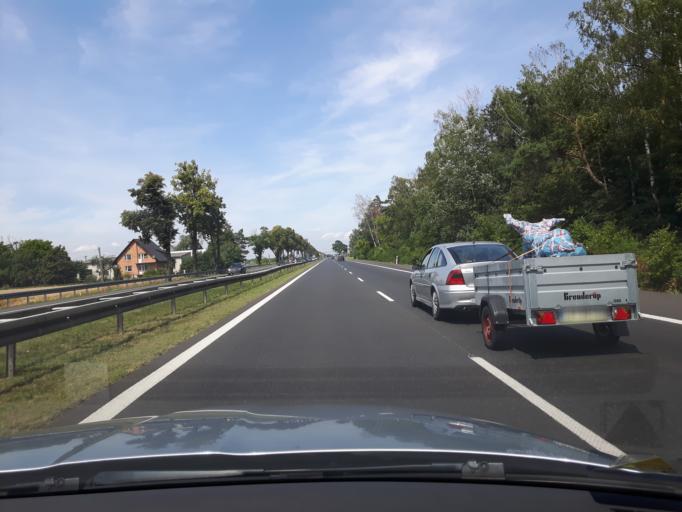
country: PL
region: Masovian Voivodeship
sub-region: Powiat nowodworski
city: Zakroczym
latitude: 52.4571
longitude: 20.5793
